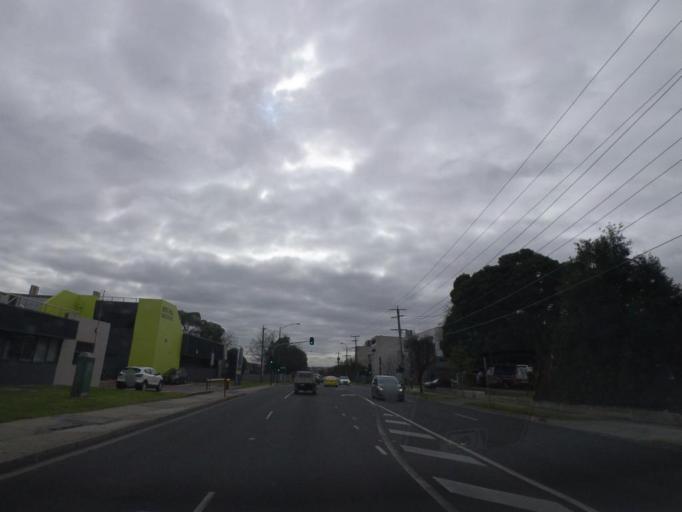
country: AU
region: Victoria
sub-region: Whitehorse
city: Box Hill
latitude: -37.8145
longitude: 145.1155
